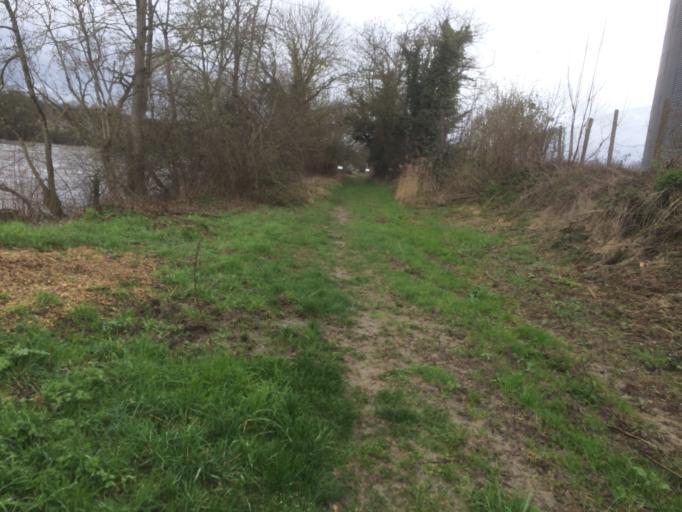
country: FR
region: Ile-de-France
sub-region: Departement de l'Essonne
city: Viry-Chatillon
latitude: 48.6671
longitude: 2.4056
